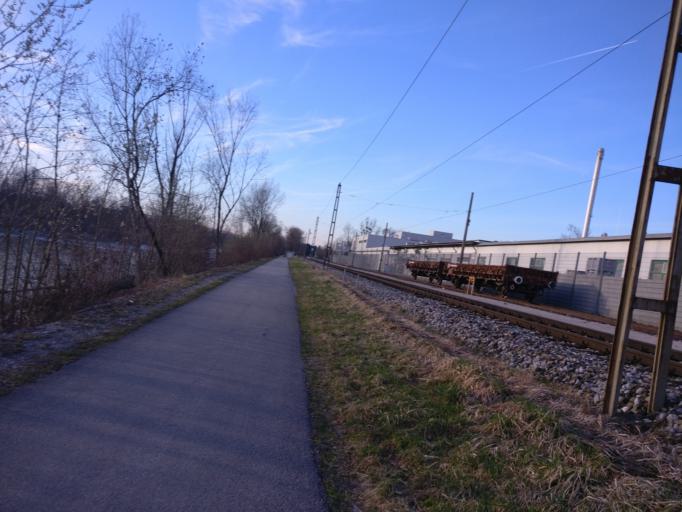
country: AT
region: Salzburg
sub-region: Politischer Bezirk Salzburg-Umgebung
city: Bergheim
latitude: 47.8443
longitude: 13.0143
